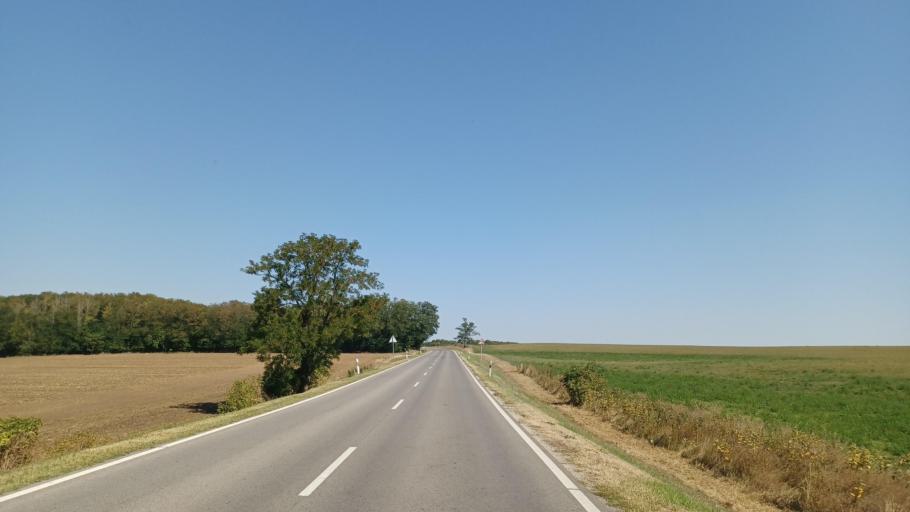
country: HU
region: Tolna
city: Nagydorog
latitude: 46.6842
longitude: 18.6704
